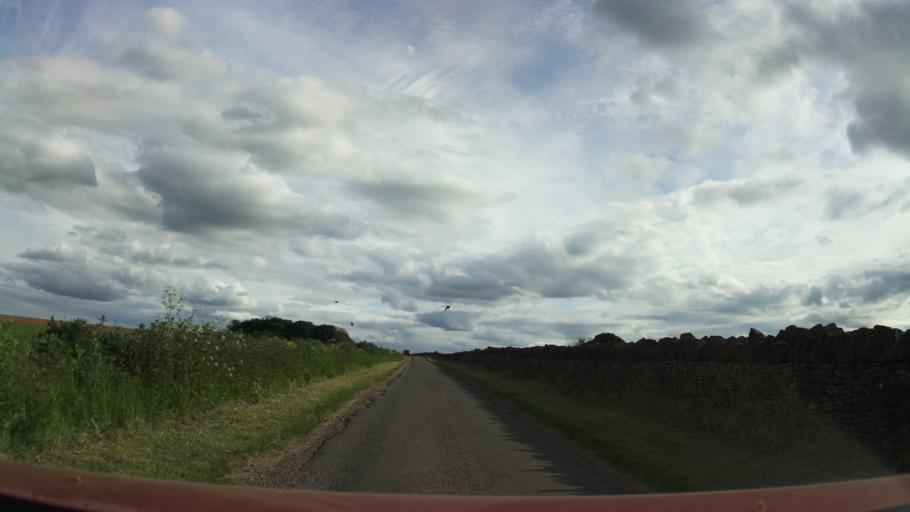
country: GB
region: England
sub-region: Gloucestershire
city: Westfield
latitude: 51.8924
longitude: -1.8869
